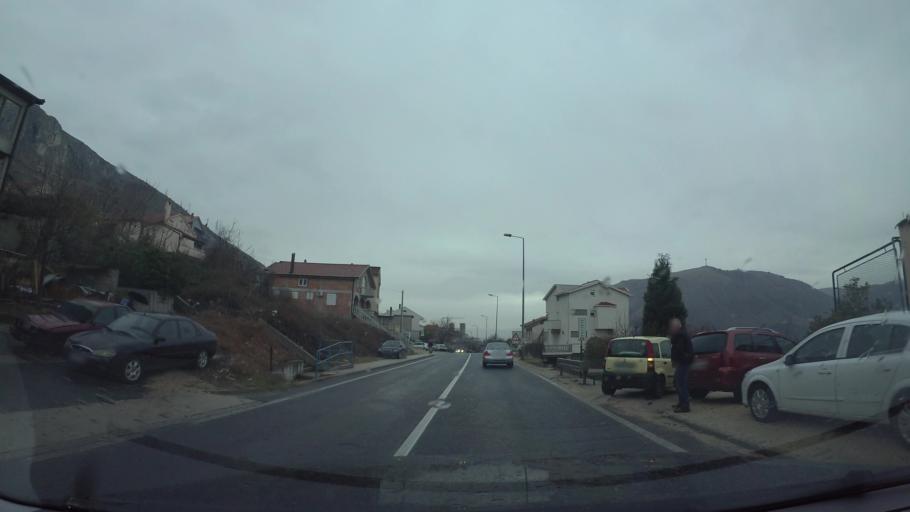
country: BA
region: Federation of Bosnia and Herzegovina
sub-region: Hercegovacko-Bosanski Kanton
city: Mostar
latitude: 43.3459
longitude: 17.8170
